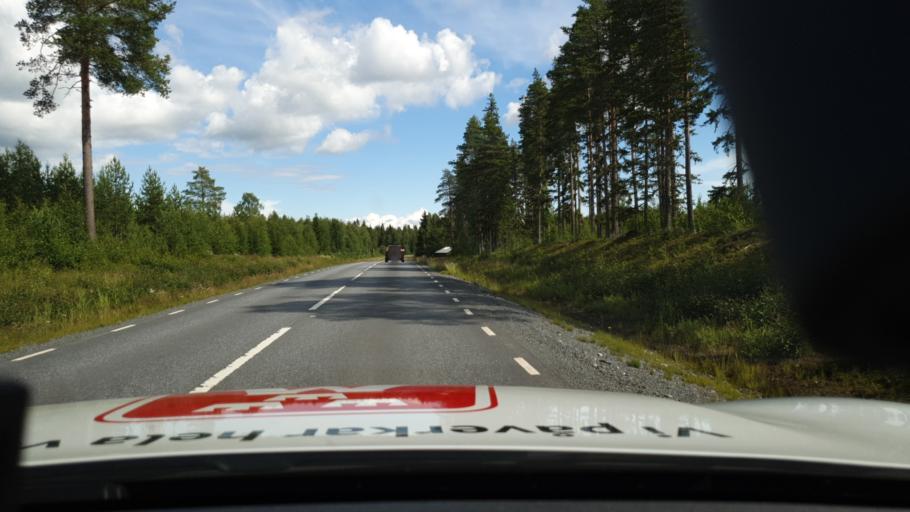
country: SE
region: Norrbotten
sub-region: Lulea Kommun
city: Gammelstad
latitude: 65.7881
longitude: 22.1103
